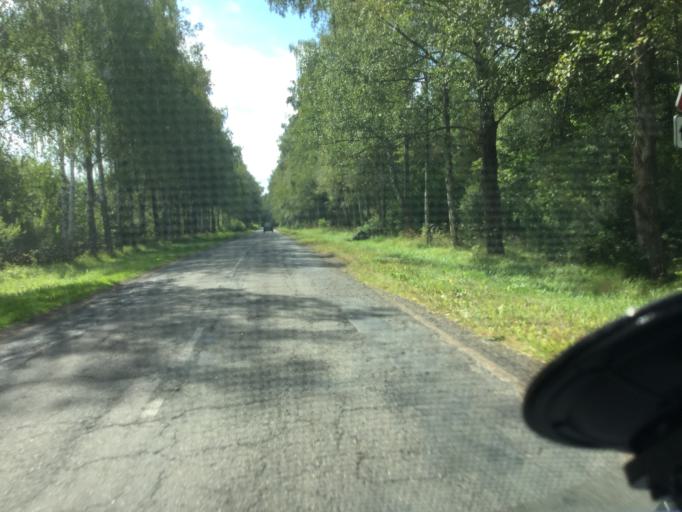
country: BY
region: Vitebsk
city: Chashniki
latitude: 55.3033
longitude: 29.3945
